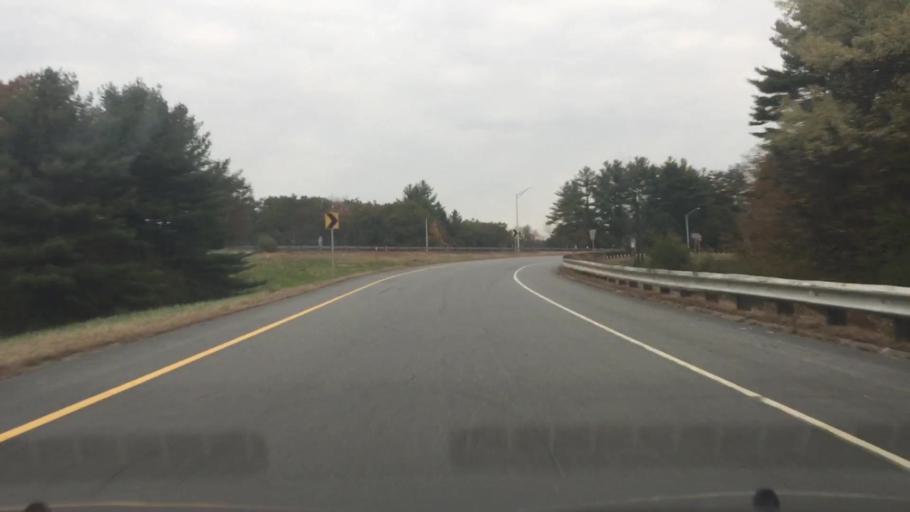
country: US
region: New Hampshire
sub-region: Cheshire County
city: Keene
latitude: 42.9435
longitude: -72.2948
